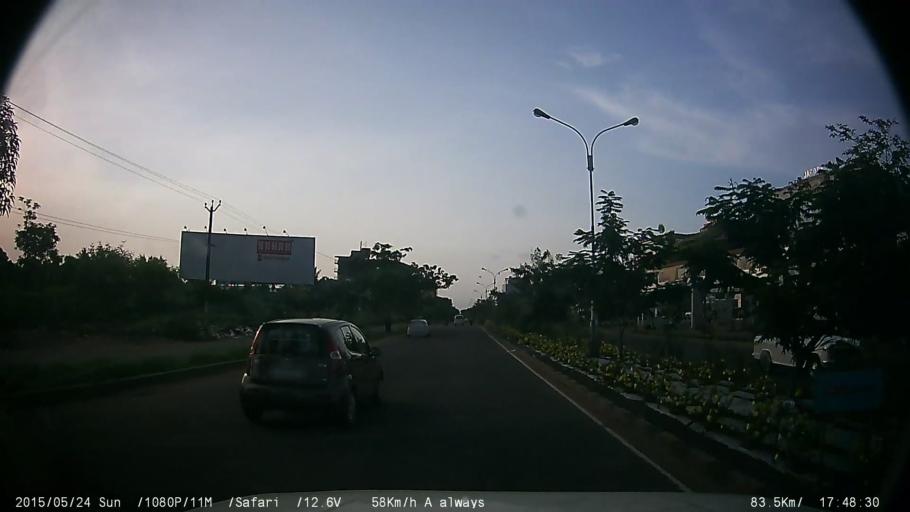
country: IN
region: Kerala
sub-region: Ernakulam
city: Cochin
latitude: 9.9823
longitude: 76.3167
